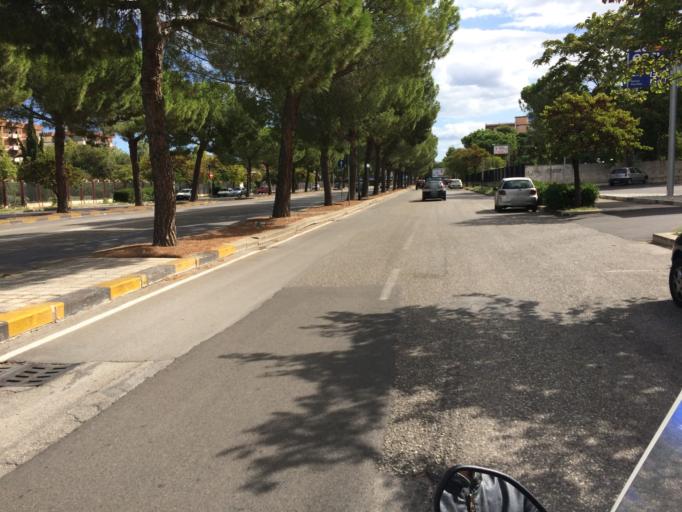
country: IT
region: Apulia
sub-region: Provincia di Bari
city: Bari
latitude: 41.0990
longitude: 16.8647
